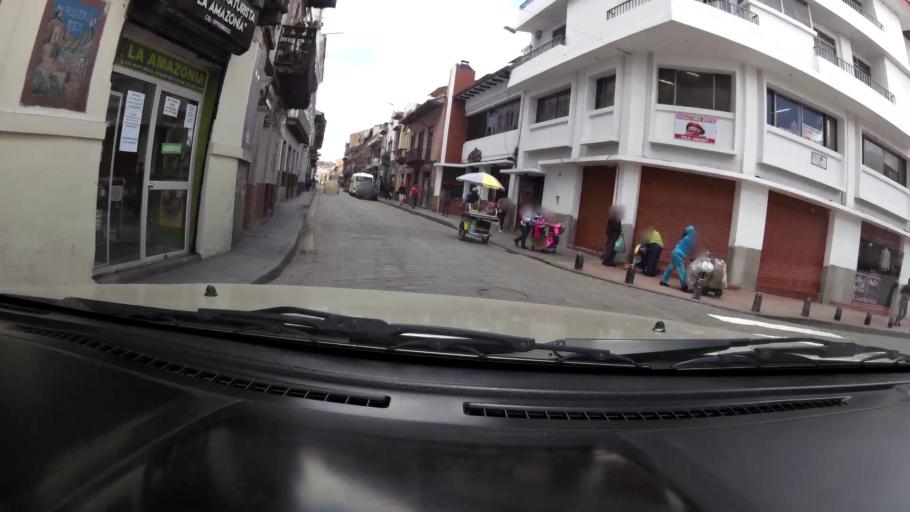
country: EC
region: Azuay
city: Cuenca
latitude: -2.8993
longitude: -79.0084
